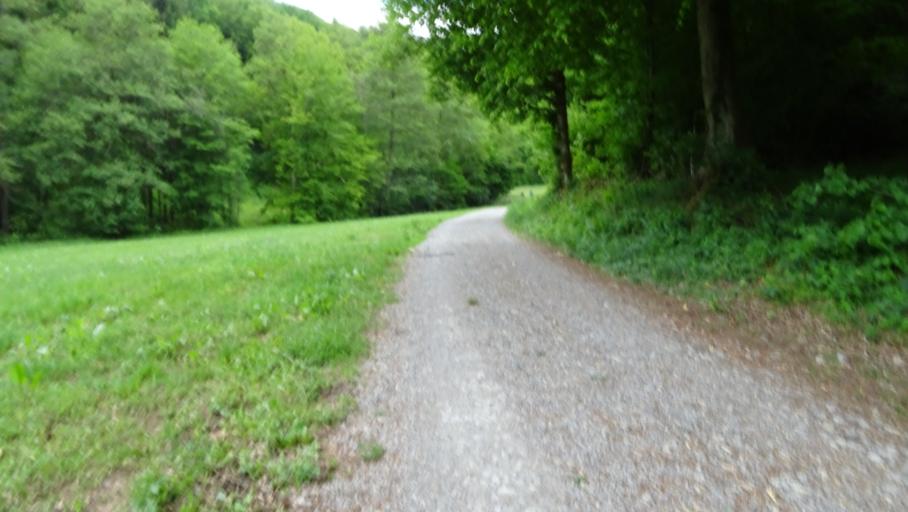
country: DE
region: Baden-Wuerttemberg
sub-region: Karlsruhe Region
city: Mosbach
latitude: 49.3891
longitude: 9.1761
